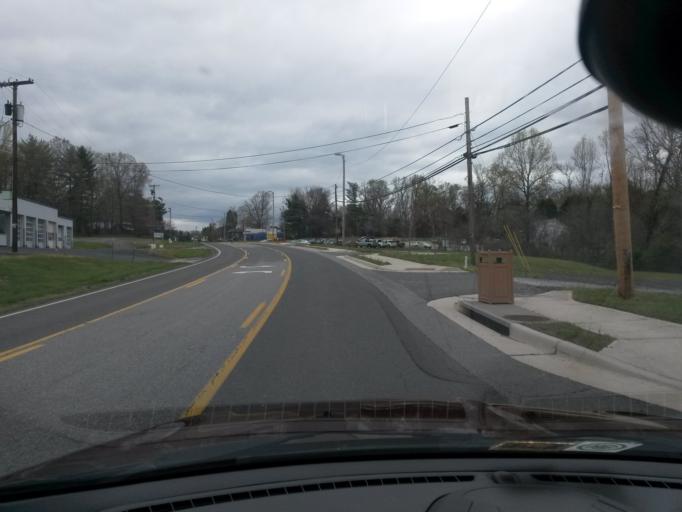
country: US
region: Virginia
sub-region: Amherst County
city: Amherst
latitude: 37.5765
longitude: -79.0570
